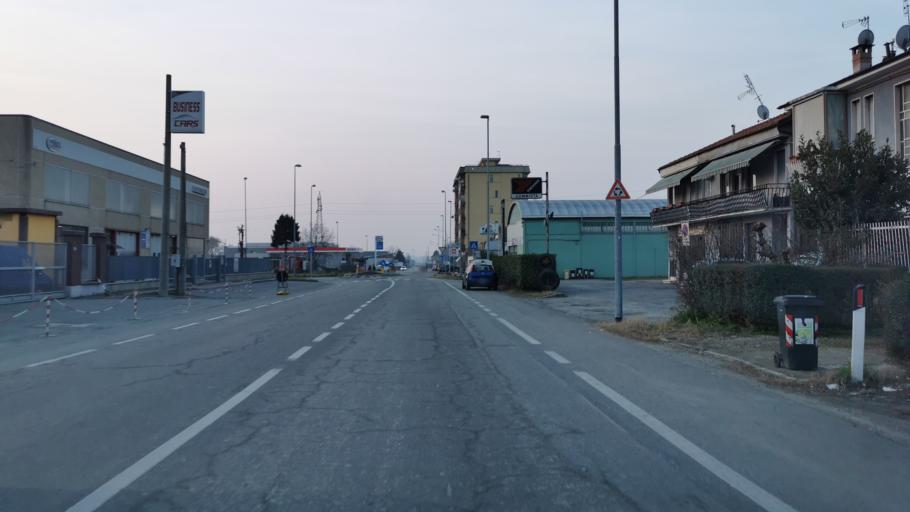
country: IT
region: Piedmont
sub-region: Provincia di Torino
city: Borgaro Torinese
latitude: 45.1477
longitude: 7.6551
